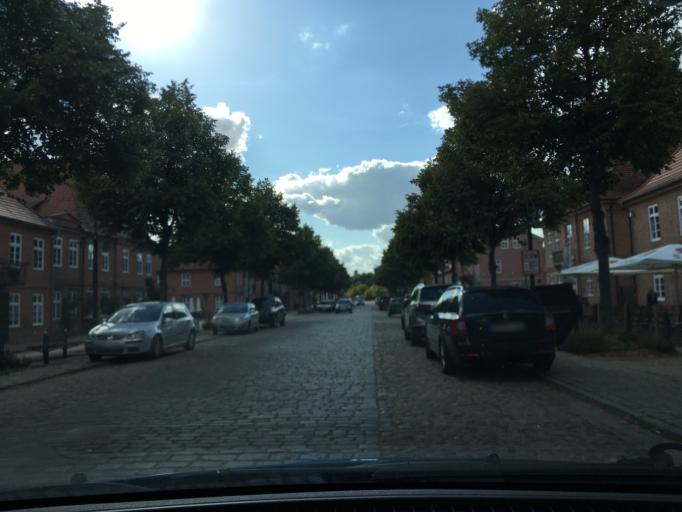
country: DE
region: Mecklenburg-Vorpommern
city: Ludwigslust
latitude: 53.3246
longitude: 11.4929
